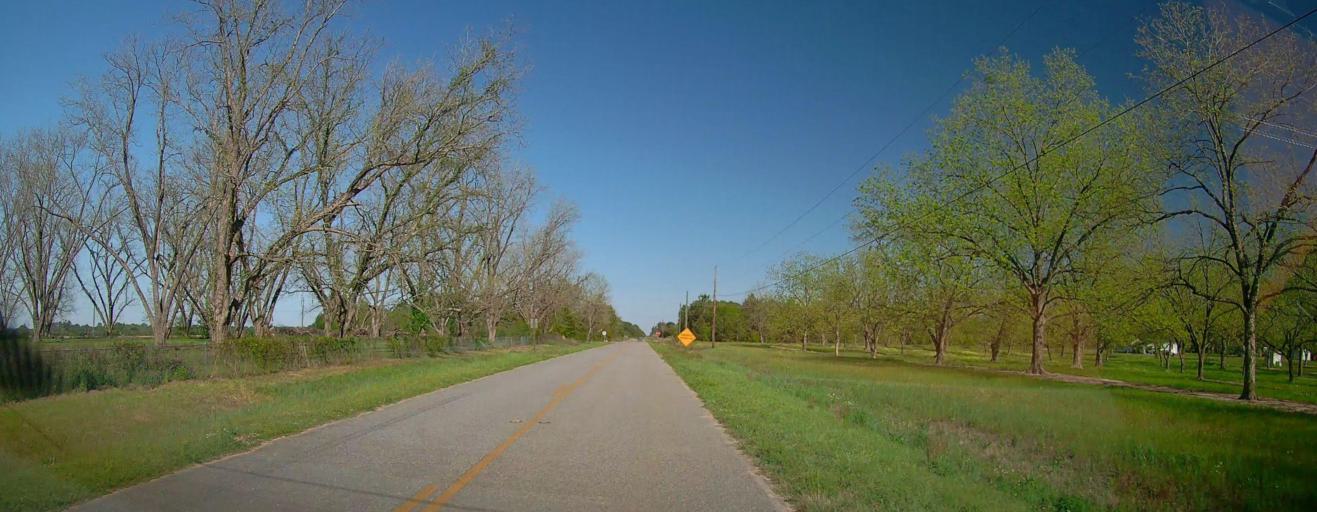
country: US
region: Georgia
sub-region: Pulaski County
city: Hawkinsville
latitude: 32.2478
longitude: -83.4749
